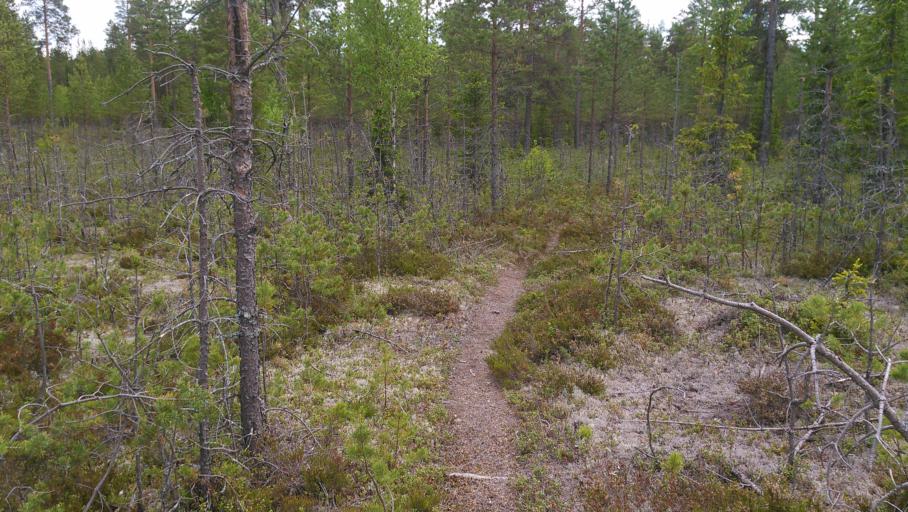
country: SE
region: Vaesterbotten
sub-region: Vannas Kommun
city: Vannasby
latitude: 64.0147
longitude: 19.9158
